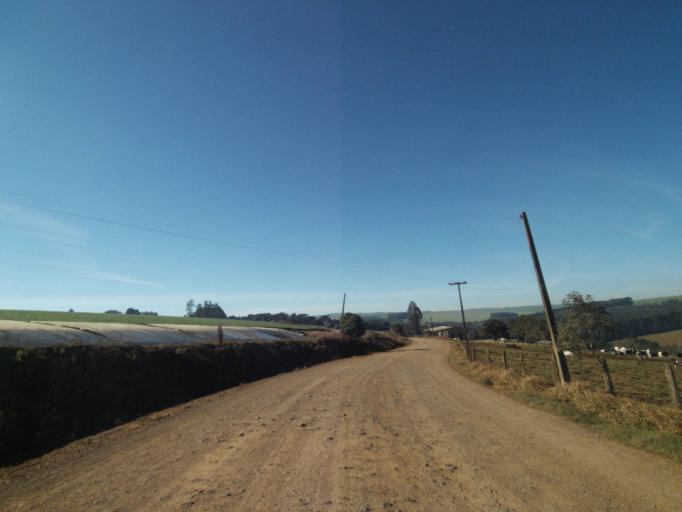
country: BR
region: Parana
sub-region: Tibagi
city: Tibagi
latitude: -24.5265
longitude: -50.3819
